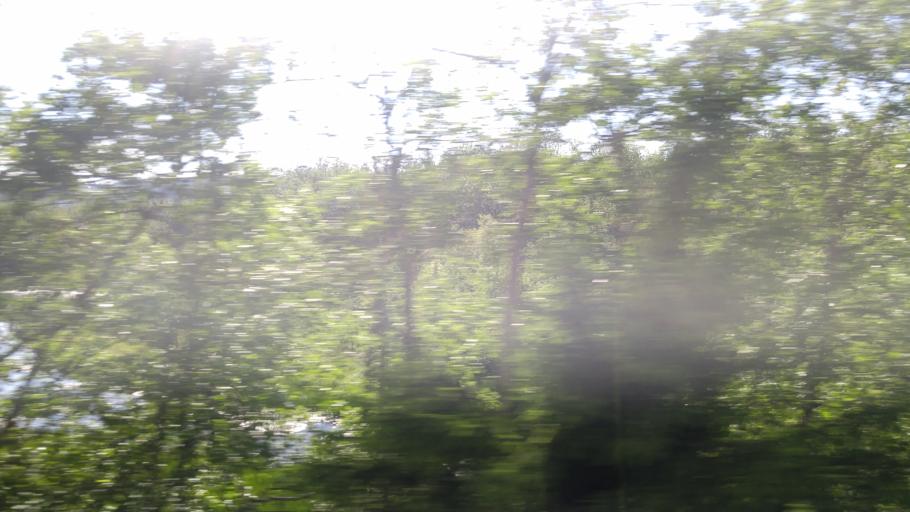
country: NO
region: Sor-Trondelag
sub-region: Melhus
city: Lundamo
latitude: 63.2148
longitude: 10.3117
